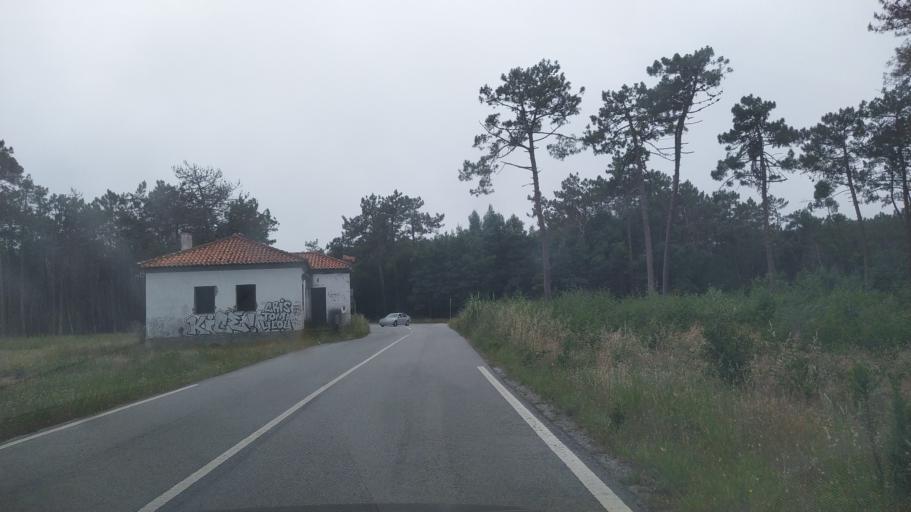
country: PT
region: Aveiro
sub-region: Ilhavo
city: Gafanha da Encarnacao
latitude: 40.5789
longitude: -8.7340
